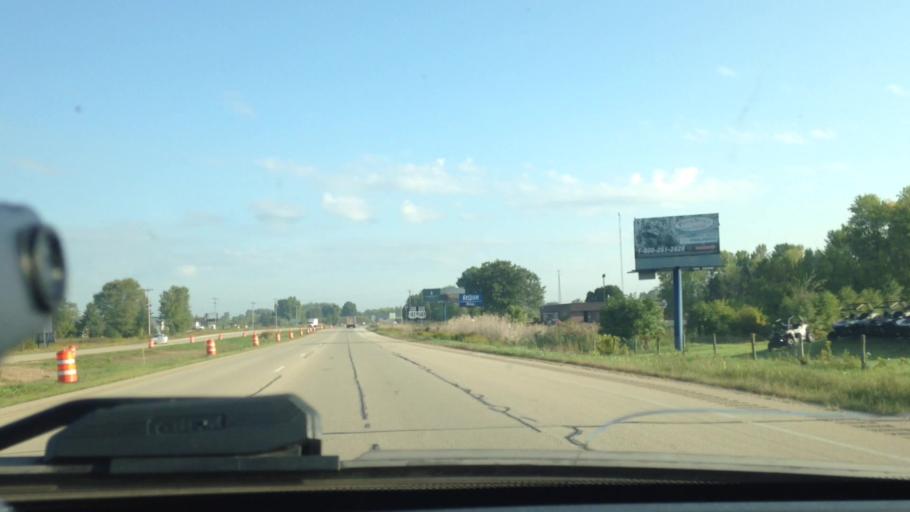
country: US
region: Wisconsin
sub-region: Oconto County
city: Oconto Falls
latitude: 44.7705
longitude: -88.0505
